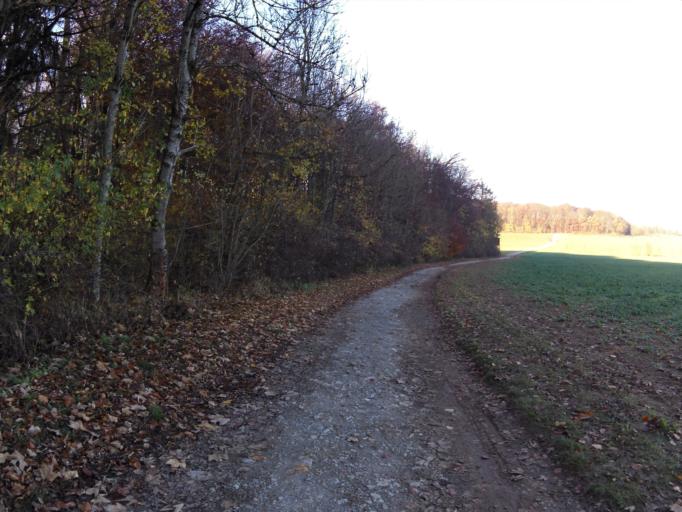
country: DE
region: Thuringia
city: Weberstedt
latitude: 51.0642
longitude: 10.4583
